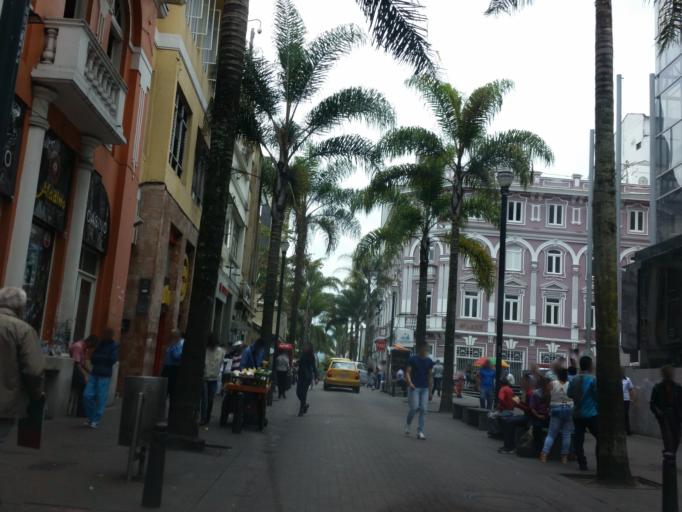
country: CO
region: Caldas
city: Manizales
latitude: 5.0670
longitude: -75.5181
